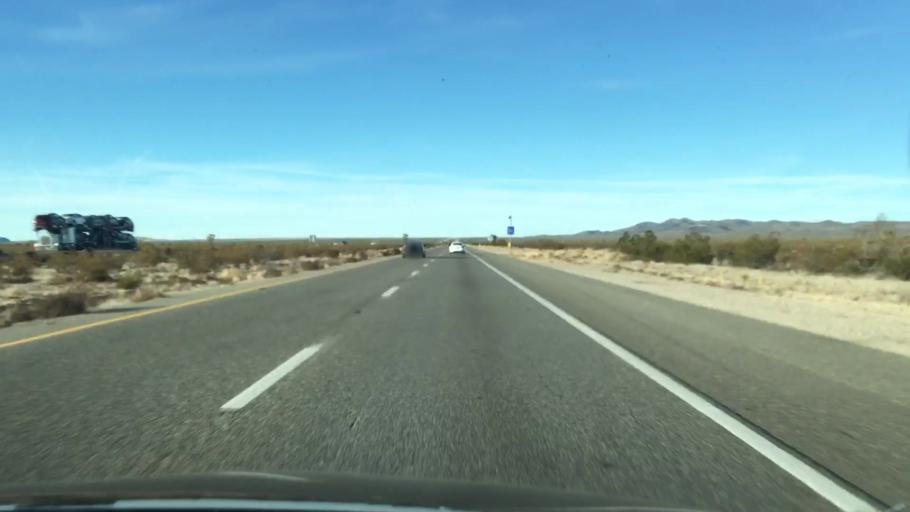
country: US
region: Nevada
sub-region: Clark County
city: Sandy Valley
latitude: 35.4286
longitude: -115.7186
